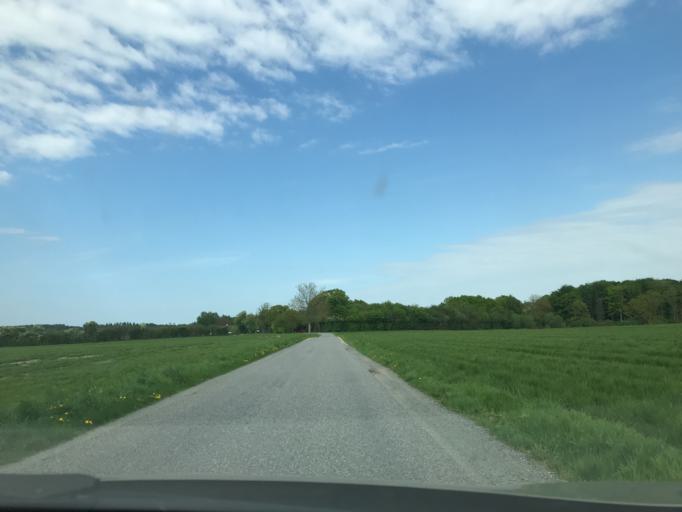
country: DK
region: South Denmark
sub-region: Middelfart Kommune
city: Norre Aby
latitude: 55.3973
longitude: 9.8592
